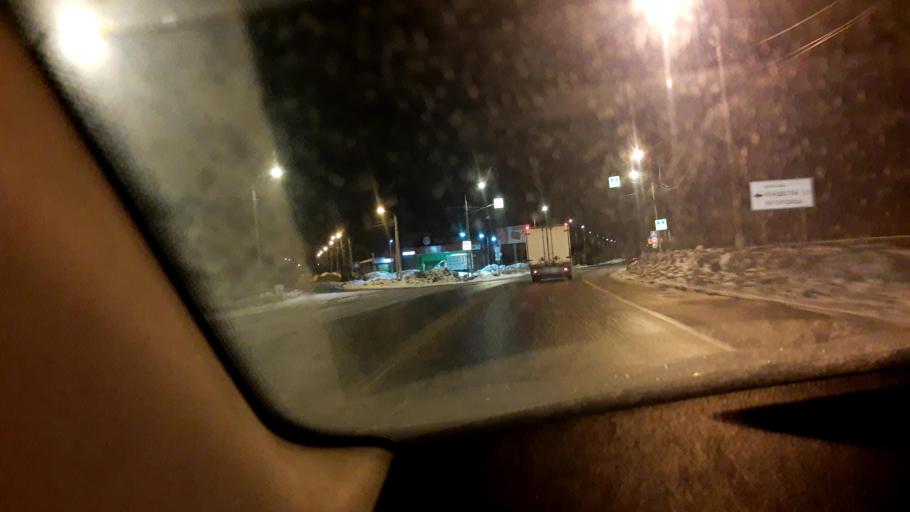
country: RU
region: Moskovskaya
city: Skoropuskovskiy
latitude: 56.3811
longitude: 38.1070
